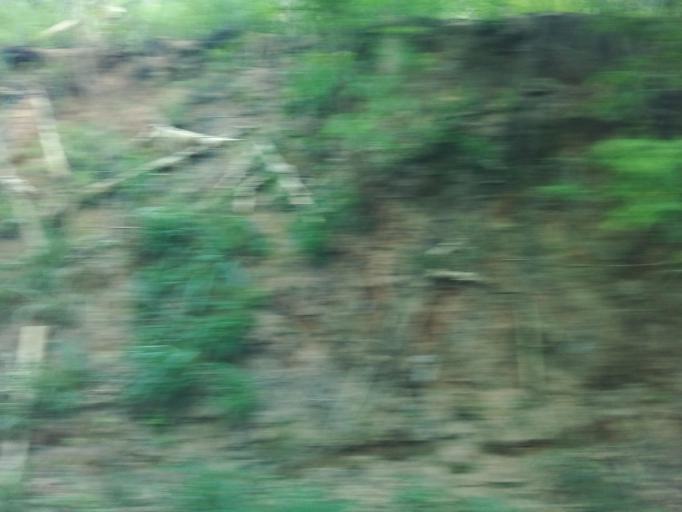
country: BR
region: Minas Gerais
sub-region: Coronel Fabriciano
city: Coronel Fabriciano
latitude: -19.5264
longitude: -42.6662
